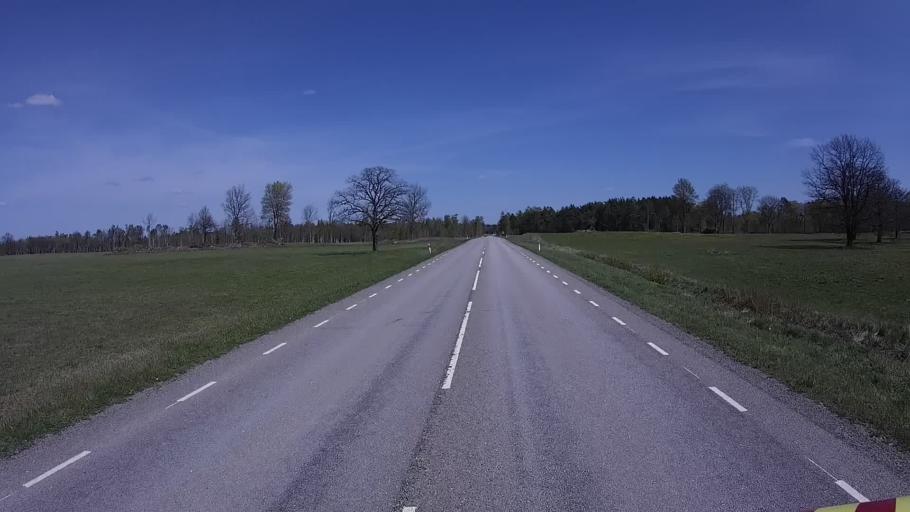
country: EE
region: Laeaene
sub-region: Ridala Parish
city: Uuemoisa
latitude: 58.9860
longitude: 23.6922
